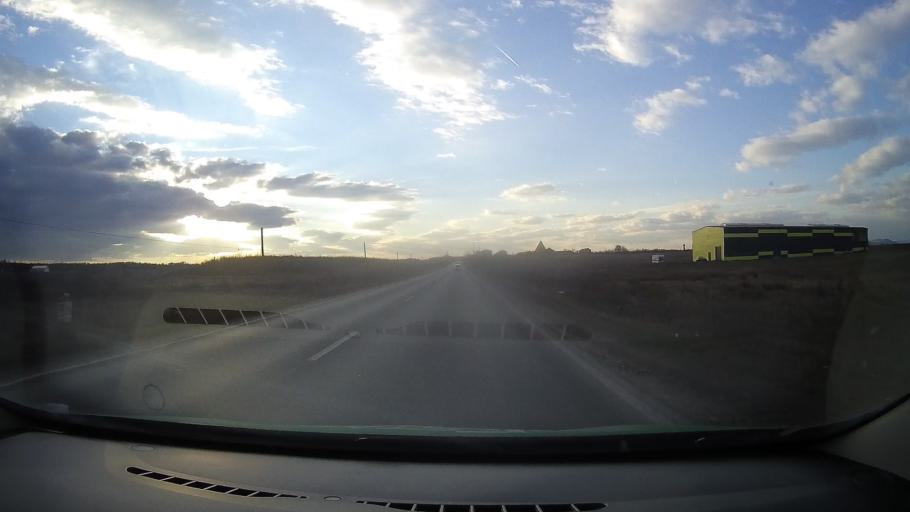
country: RO
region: Dambovita
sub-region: Comuna I. L. Caragiale
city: Mija
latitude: 44.9111
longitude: 25.6861
